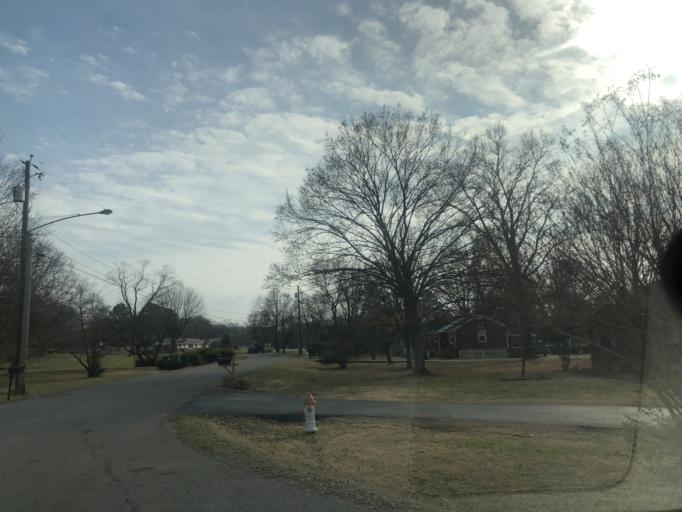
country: US
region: Tennessee
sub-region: Davidson County
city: Oak Hill
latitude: 36.1051
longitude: -86.7080
